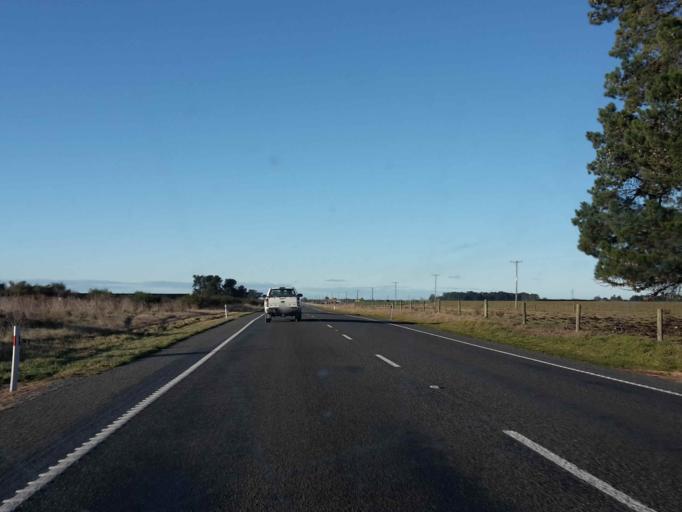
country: NZ
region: Canterbury
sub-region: Ashburton District
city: Tinwald
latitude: -44.0236
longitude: 171.5028
